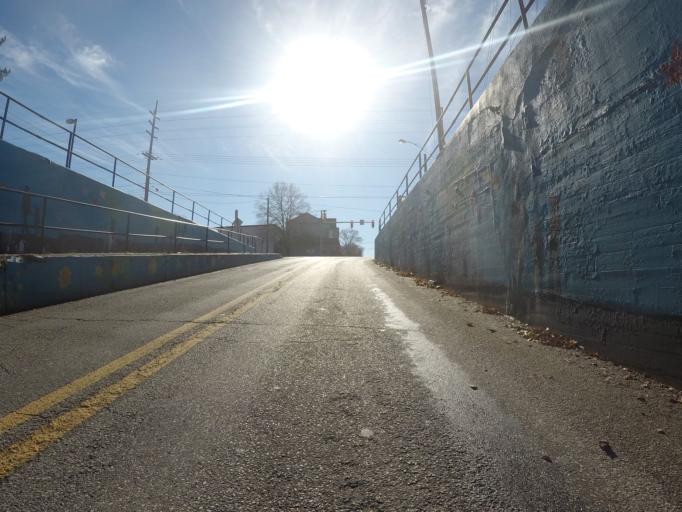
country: US
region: West Virginia
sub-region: Cabell County
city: Huntington
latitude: 38.4158
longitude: -82.4405
